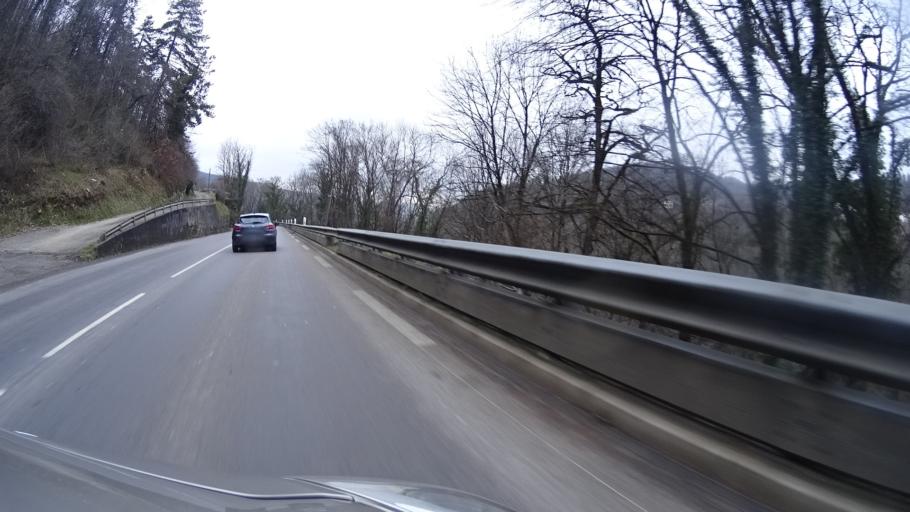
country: FR
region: Franche-Comte
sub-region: Departement du Doubs
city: Morre
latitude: 47.2285
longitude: 6.0623
